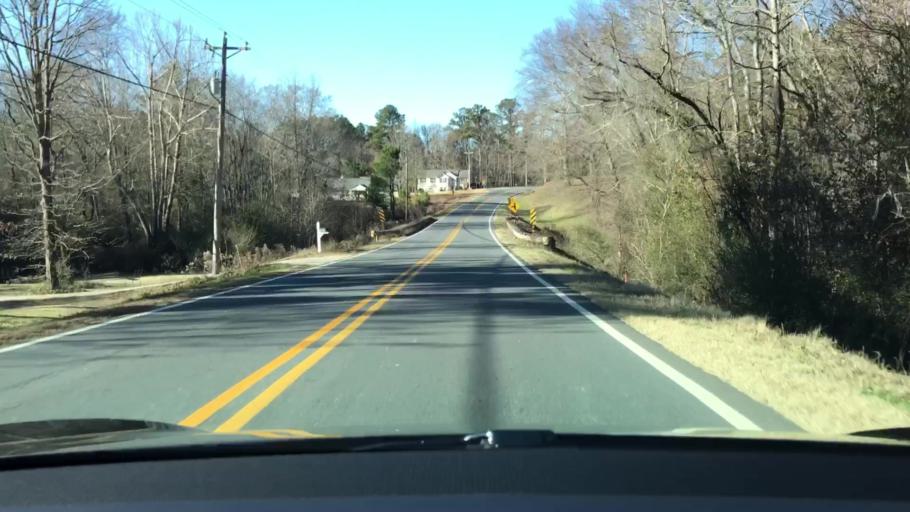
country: US
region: Georgia
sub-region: Barrow County
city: Auburn
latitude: 33.9802
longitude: -83.7934
